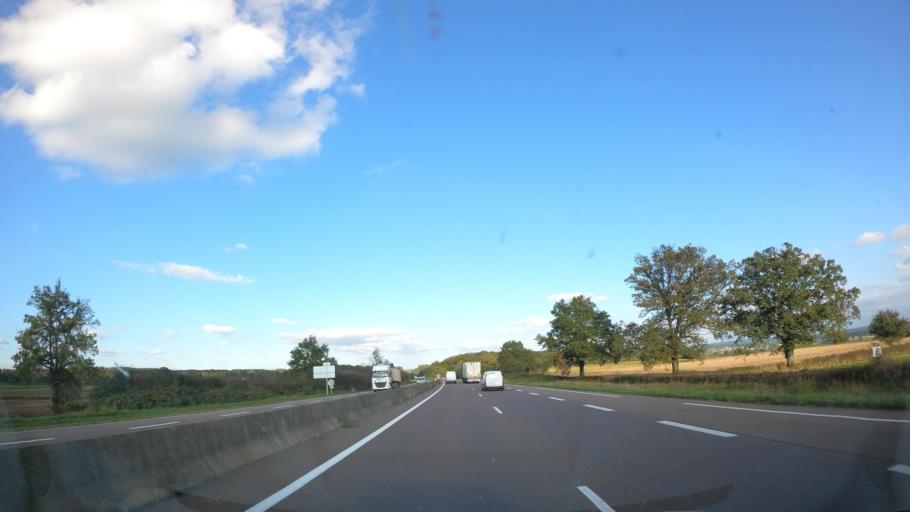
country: FR
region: Bourgogne
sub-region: Departement de Saone-et-Loire
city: Ciry-le-Noble
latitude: 46.6248
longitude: 4.3008
